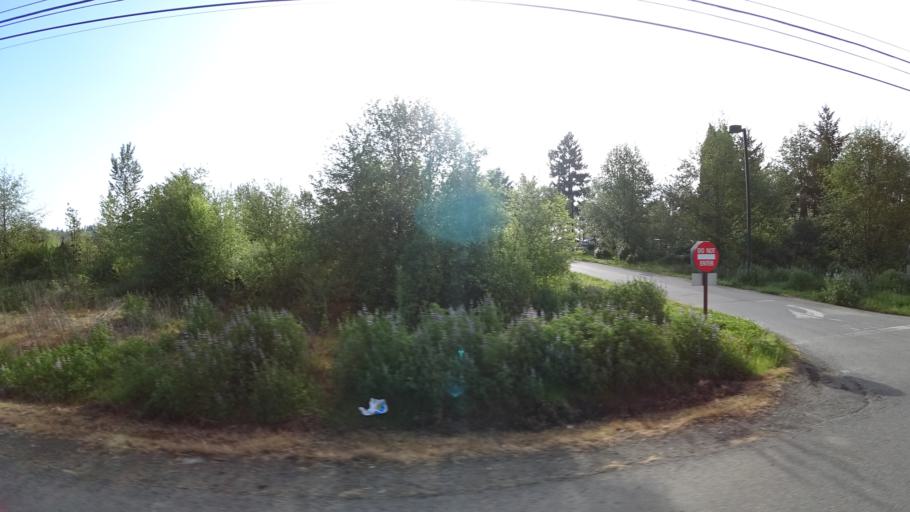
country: US
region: Oregon
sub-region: Washington County
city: Hillsboro
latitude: 45.5029
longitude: -122.9909
